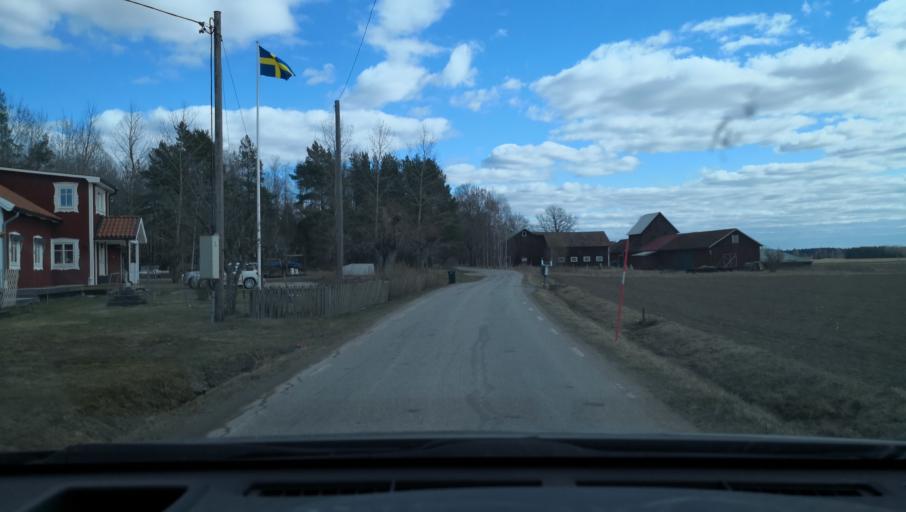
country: SE
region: Vaestmanland
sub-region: Sala Kommun
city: Sala
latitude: 59.8617
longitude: 16.5971
